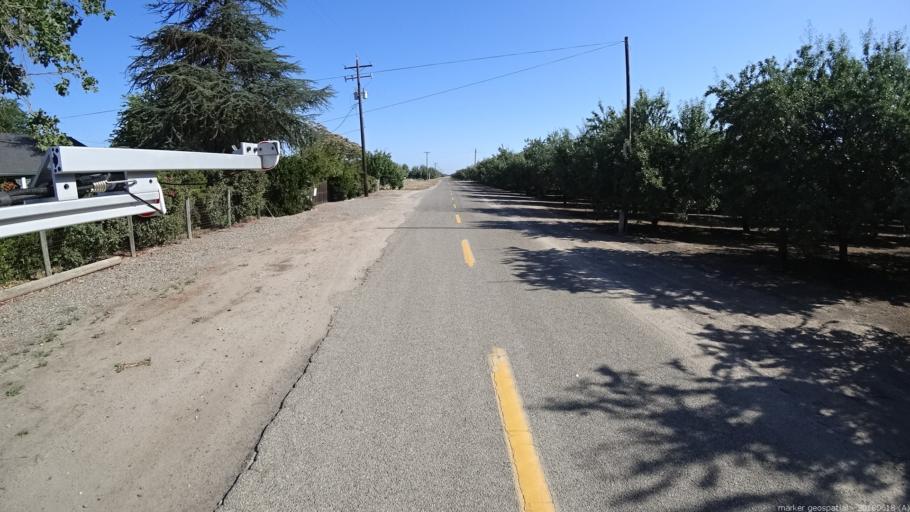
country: US
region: California
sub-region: Madera County
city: Madera
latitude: 36.9044
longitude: -120.1377
